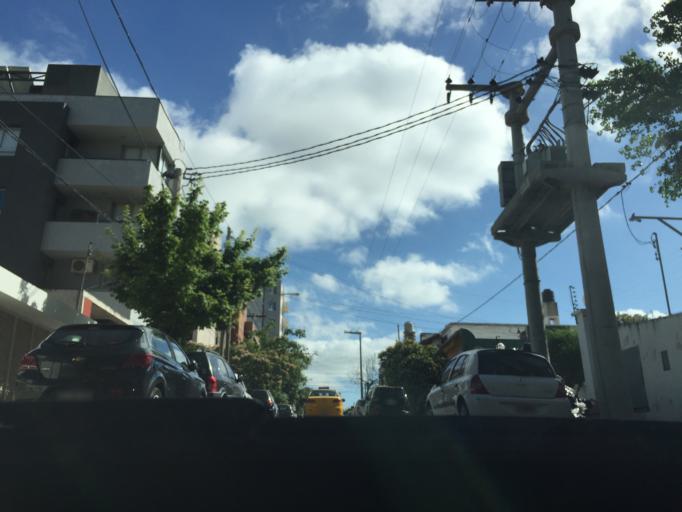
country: AR
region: Cordoba
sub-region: Departamento de Capital
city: Cordoba
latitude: -31.4037
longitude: -64.2003
